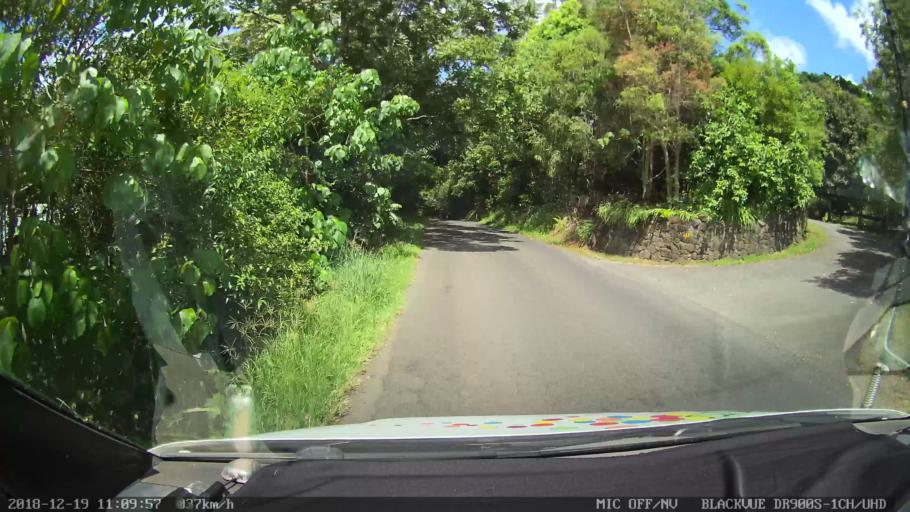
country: AU
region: New South Wales
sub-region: Lismore Municipality
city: Nimbin
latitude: -28.6354
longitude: 153.2621
